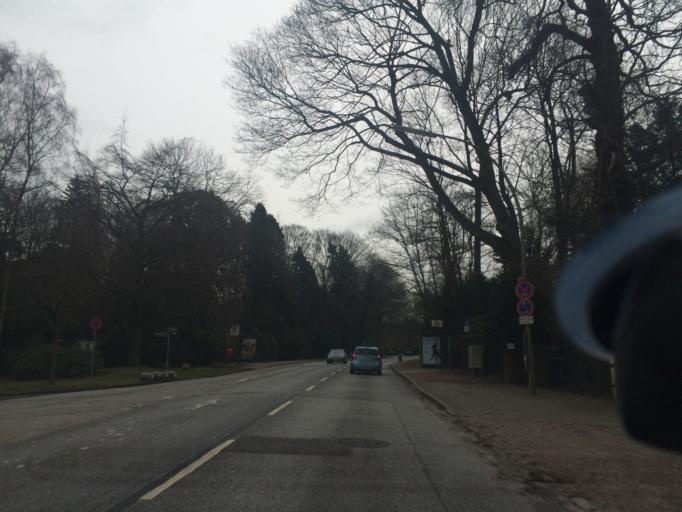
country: DE
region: Hamburg
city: Altona
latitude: 53.5472
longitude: 9.8733
